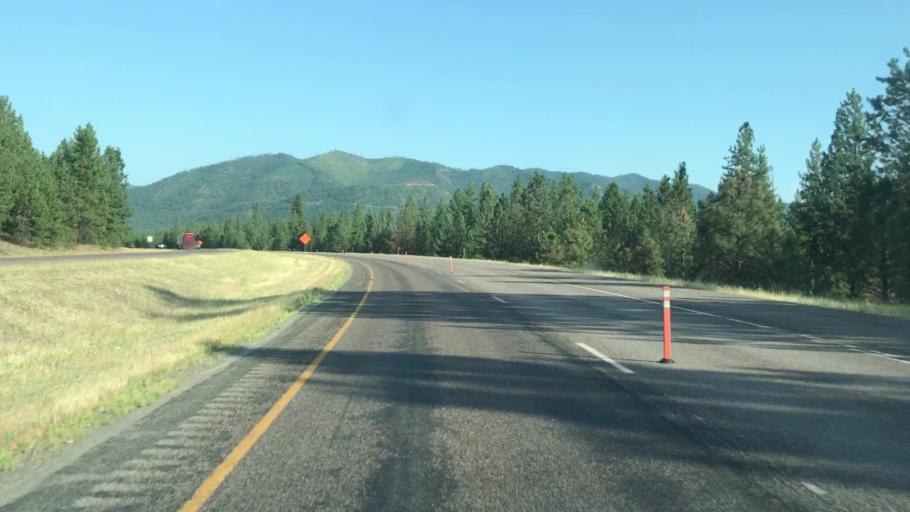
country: US
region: Montana
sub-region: Mineral County
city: Superior
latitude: 47.0163
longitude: -114.7346
